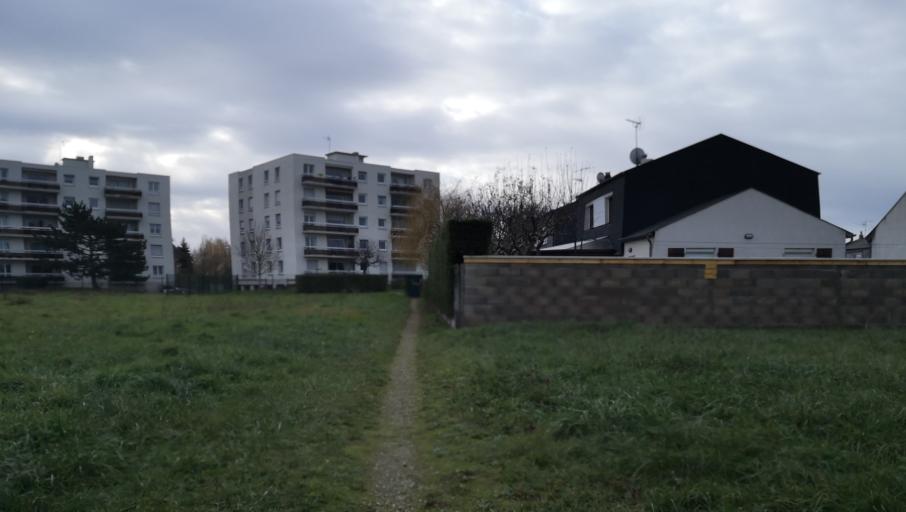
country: FR
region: Centre
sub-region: Departement du Loiret
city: Saint-Jean-de-Braye
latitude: 47.9104
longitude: 1.9568
